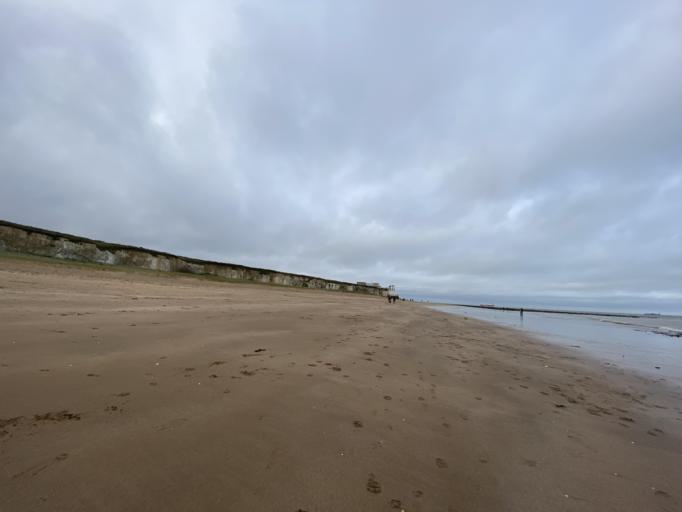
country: GB
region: England
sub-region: Kent
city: Broadstairs
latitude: 51.3921
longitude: 1.4305
